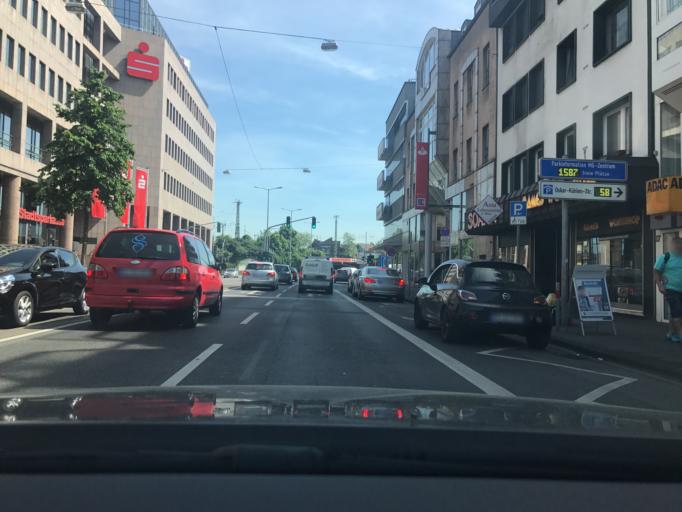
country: DE
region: North Rhine-Westphalia
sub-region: Regierungsbezirk Dusseldorf
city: Monchengladbach
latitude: 51.1954
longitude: 6.4427
